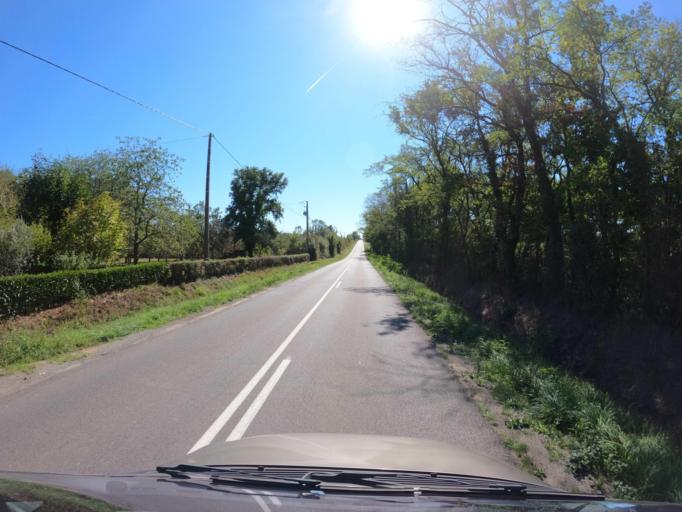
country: FR
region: Poitou-Charentes
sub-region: Departement de la Vienne
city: Lathus-Saint-Remy
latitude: 46.3654
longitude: 0.9387
